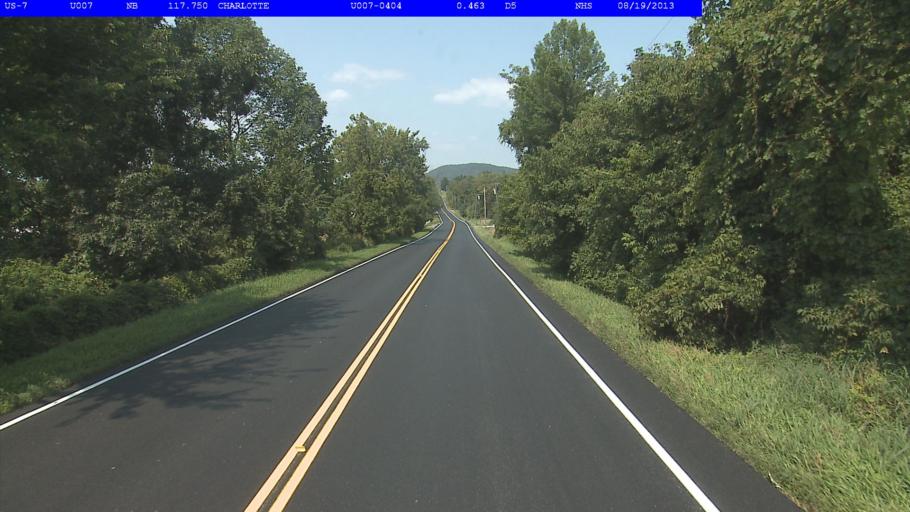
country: US
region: Vermont
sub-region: Addison County
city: Vergennes
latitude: 44.2689
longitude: -73.2331
